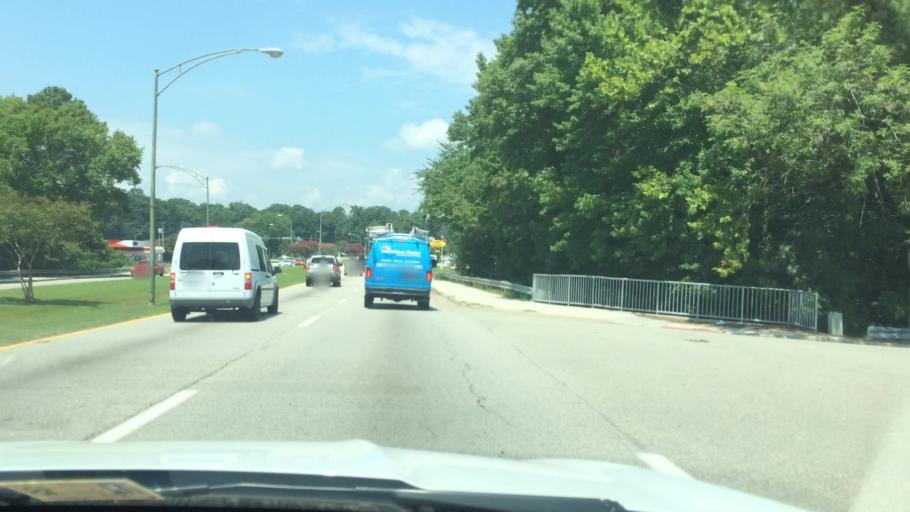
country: US
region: Virginia
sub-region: York County
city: Yorktown
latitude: 37.1316
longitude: -76.5404
